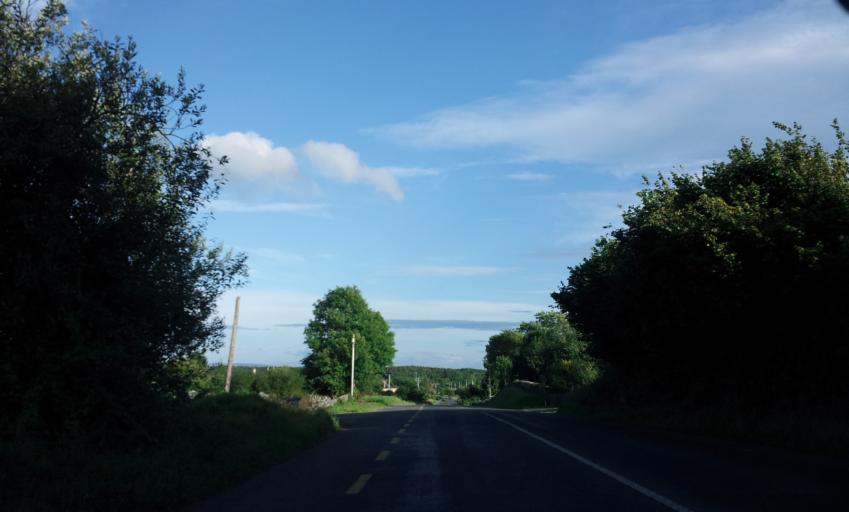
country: IE
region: Munster
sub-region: An Clar
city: Ennis
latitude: 52.8731
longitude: -9.0330
